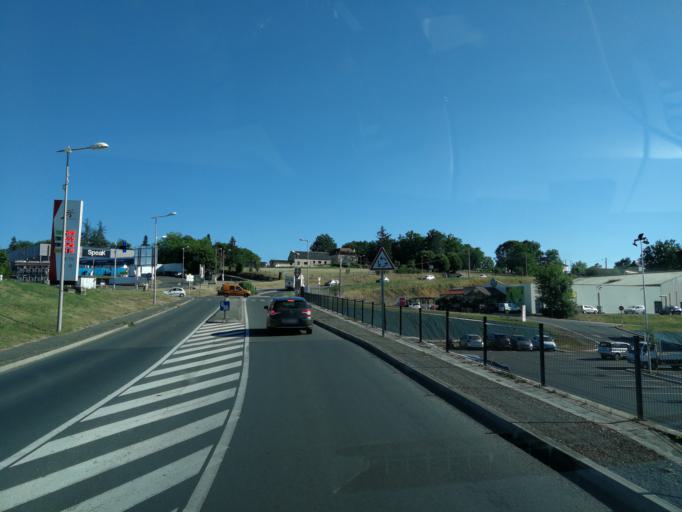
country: FR
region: Midi-Pyrenees
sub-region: Departement du Lot
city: Gourdon
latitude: 44.7258
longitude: 1.3725
